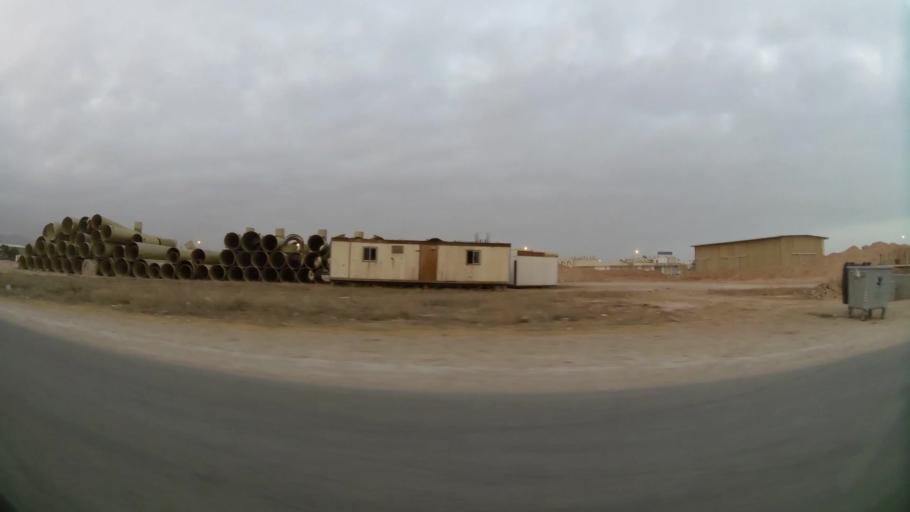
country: OM
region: Zufar
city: Salalah
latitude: 17.0271
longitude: 54.0336
